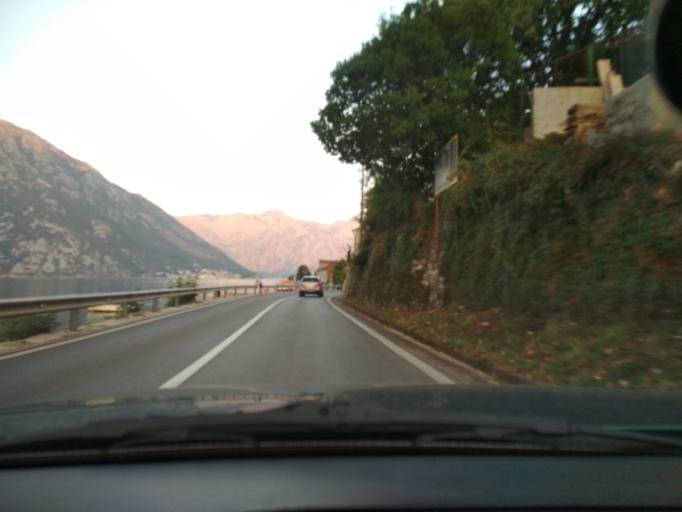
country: ME
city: Lipci
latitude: 42.4868
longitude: 18.6635
